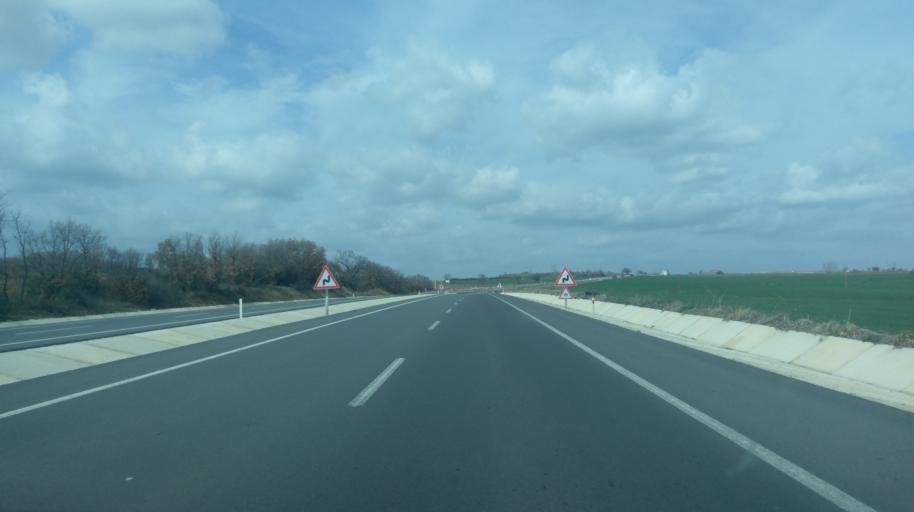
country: TR
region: Edirne
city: Kesan
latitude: 40.9012
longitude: 26.6328
